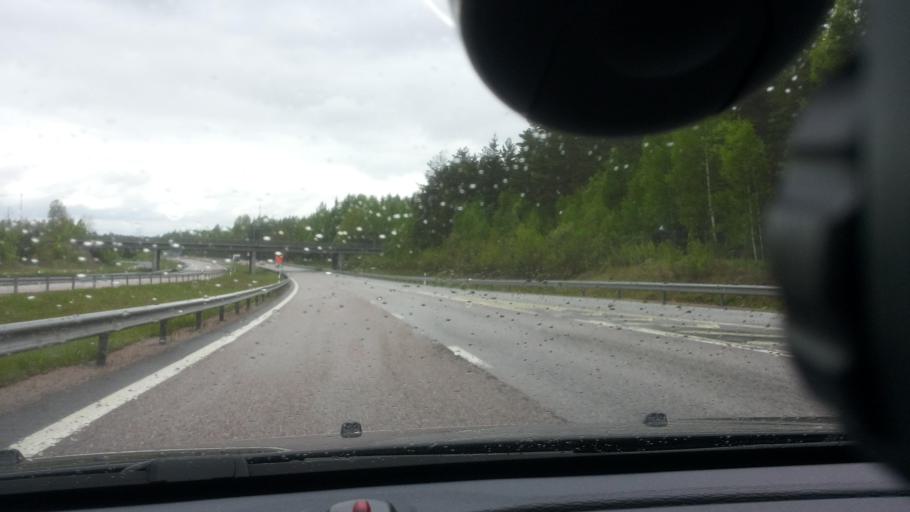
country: SE
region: Uppsala
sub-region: Alvkarleby Kommun
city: AElvkarleby
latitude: 60.4650
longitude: 17.4110
